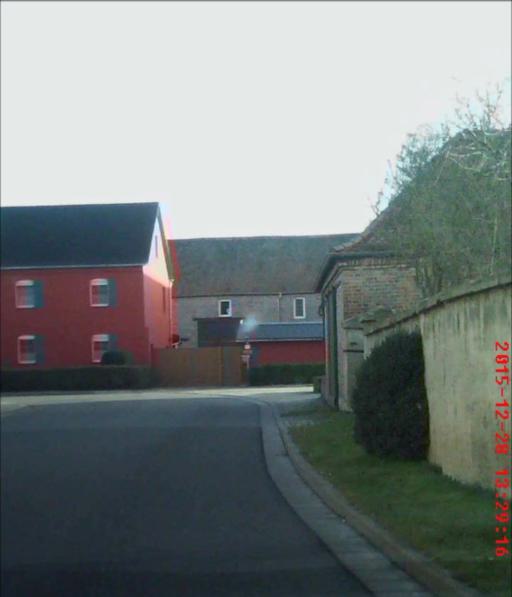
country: DE
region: Thuringia
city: Eberstedt
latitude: 51.0712
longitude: 11.5857
